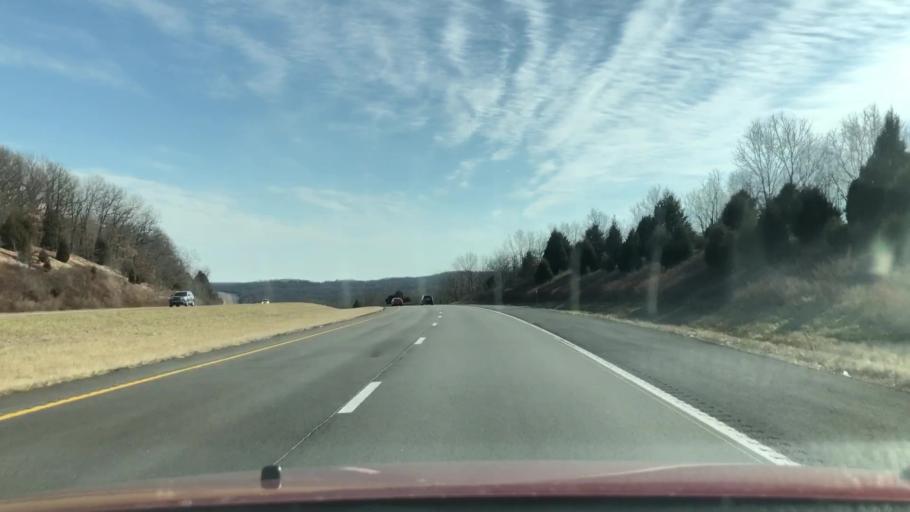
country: US
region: Missouri
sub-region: Wright County
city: Mansfield
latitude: 37.1137
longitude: -92.6713
